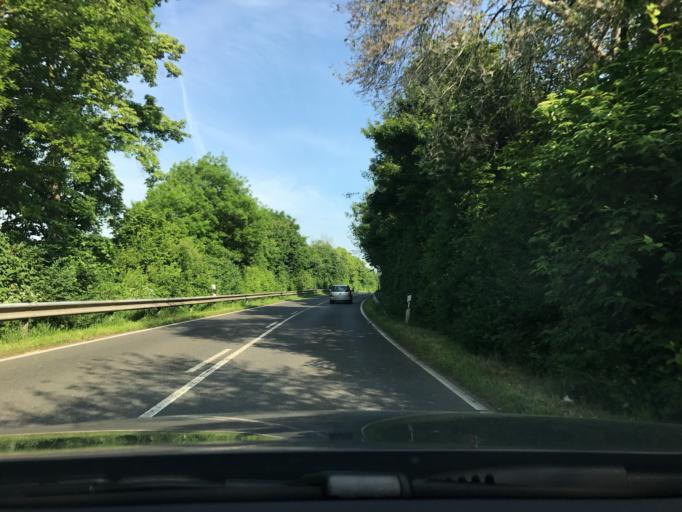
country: DE
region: North Rhine-Westphalia
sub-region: Regierungsbezirk Dusseldorf
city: Kamp-Lintfort
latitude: 51.4263
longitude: 6.5445
